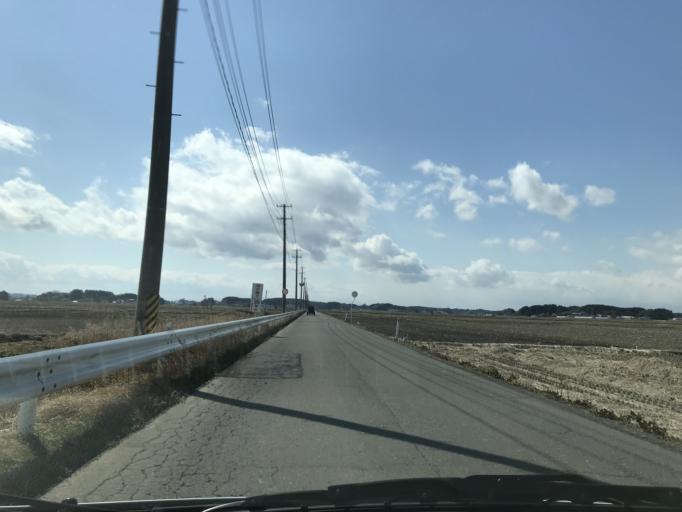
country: JP
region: Miyagi
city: Wakuya
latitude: 38.6840
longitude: 141.1662
